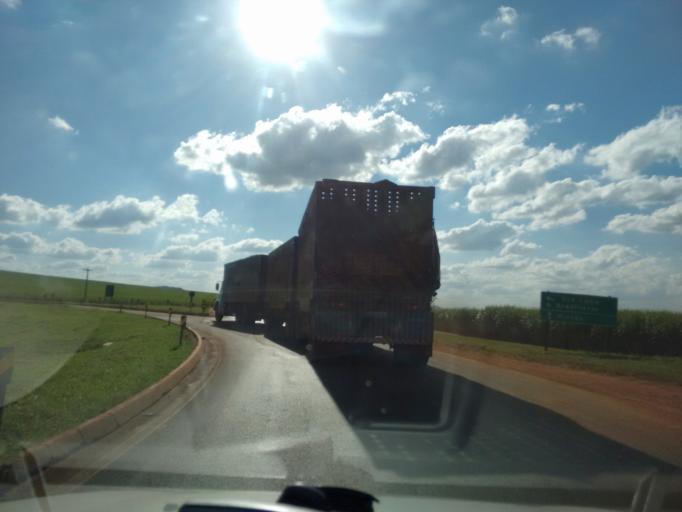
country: BR
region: Sao Paulo
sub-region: Americo Brasiliense
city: Americo Brasiliense
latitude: -21.6133
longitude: -48.0321
